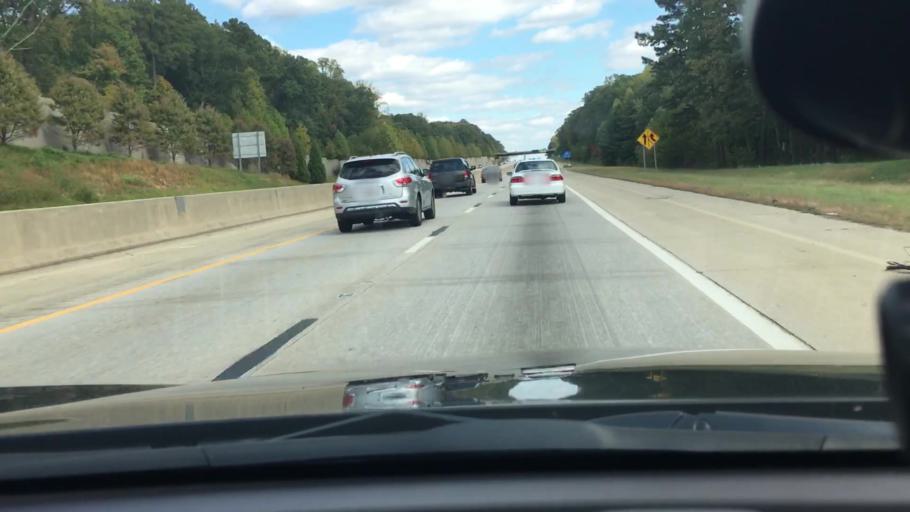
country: US
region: North Carolina
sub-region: Wake County
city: Cary
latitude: 35.7394
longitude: -78.7887
